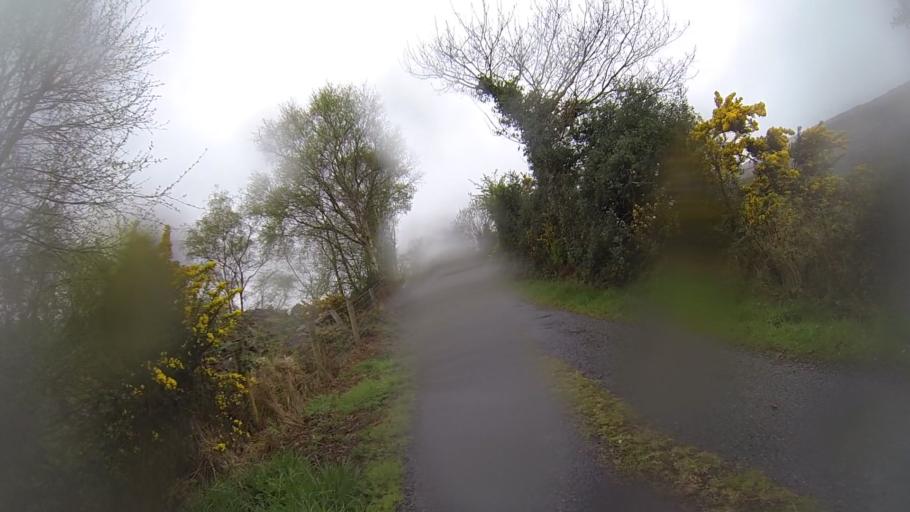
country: IE
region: Munster
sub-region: Ciarrai
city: Kenmare
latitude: 51.8252
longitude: -9.5255
